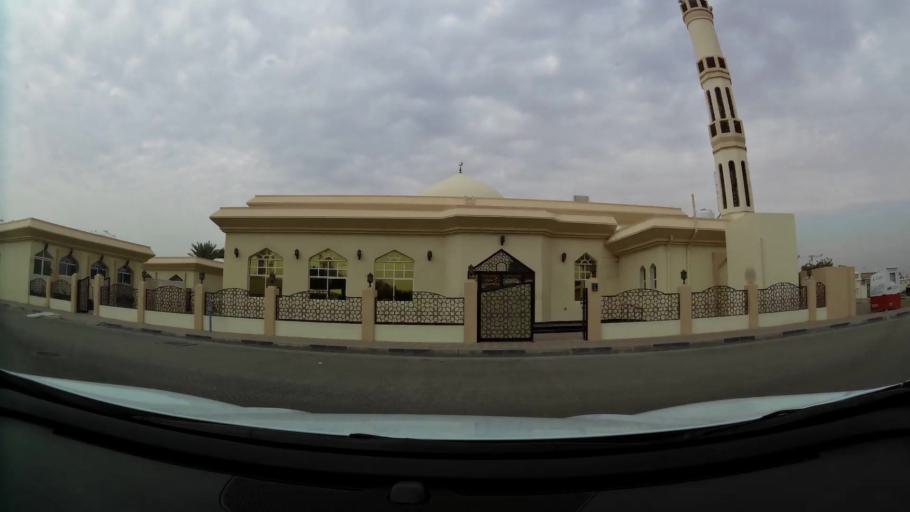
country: AE
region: Abu Dhabi
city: Al Ain
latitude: 24.2264
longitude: 55.7417
